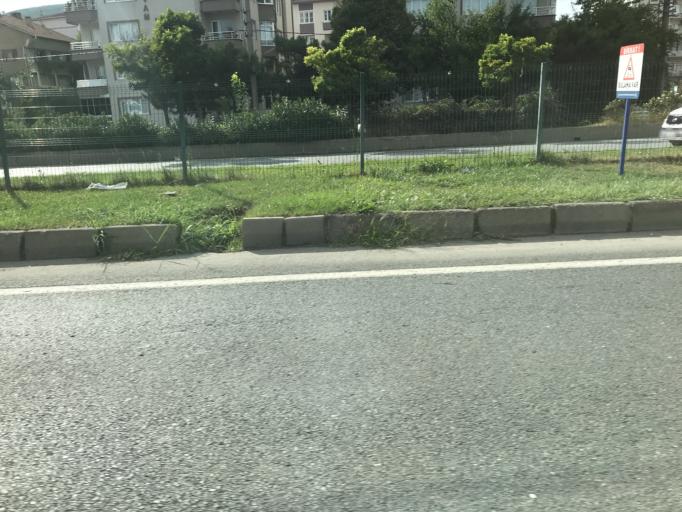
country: TR
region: Bursa
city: Orhangazi
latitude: 40.4840
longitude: 29.3100
